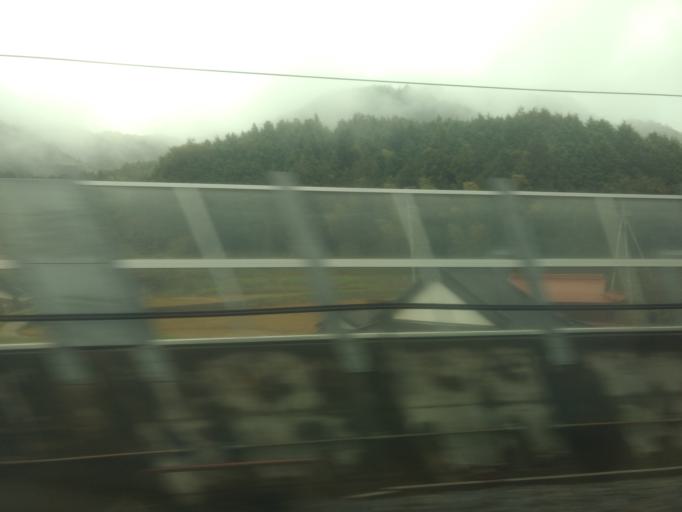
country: JP
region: Yamaguchi
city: Yanai
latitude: 34.0954
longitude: 132.0403
